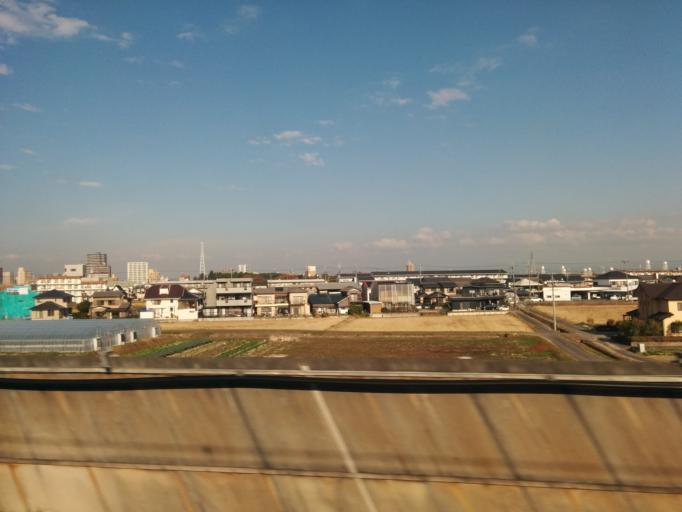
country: JP
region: Aichi
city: Anjo
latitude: 34.9446
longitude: 137.0831
